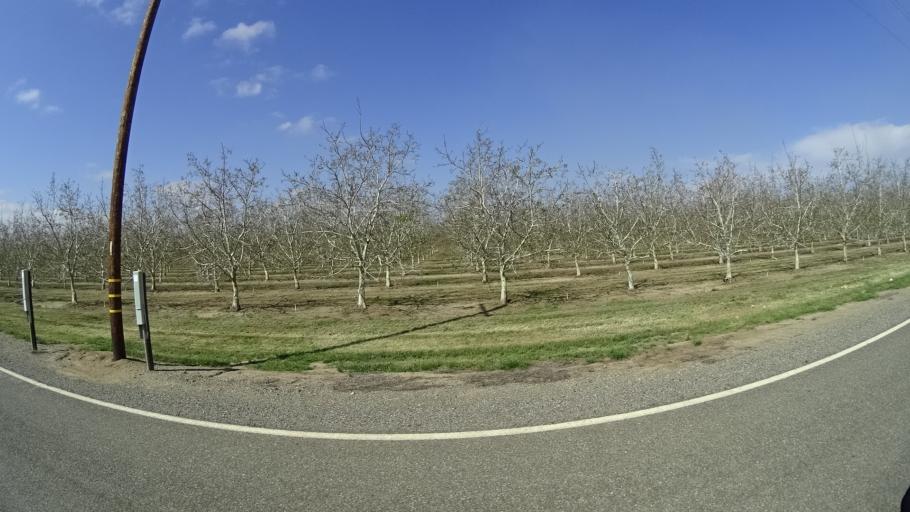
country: US
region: California
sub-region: Butte County
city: Biggs
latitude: 39.4470
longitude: -121.9303
